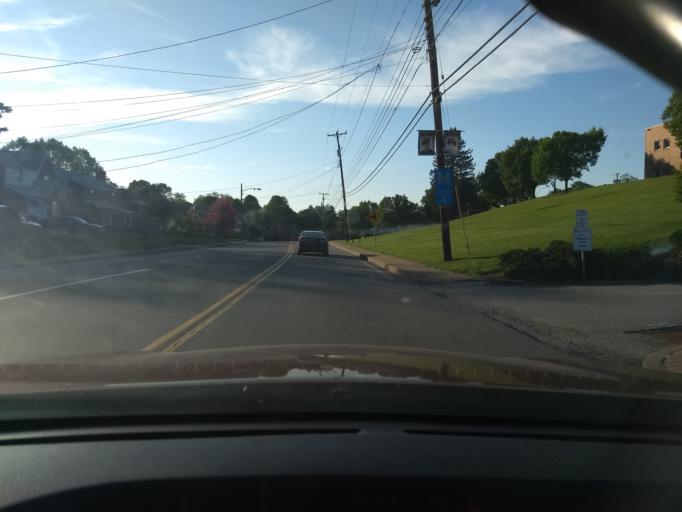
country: US
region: Pennsylvania
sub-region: Allegheny County
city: White Oak
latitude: 40.3483
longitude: -79.8330
